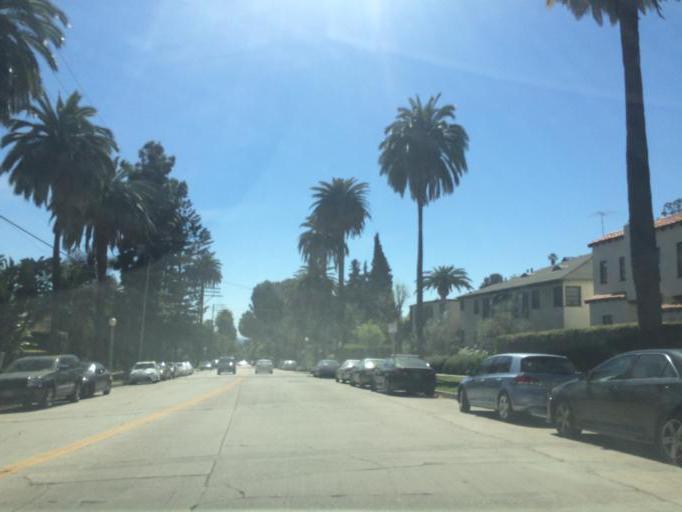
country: US
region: California
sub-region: Los Angeles County
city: Hollywood
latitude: 34.1125
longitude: -118.3215
